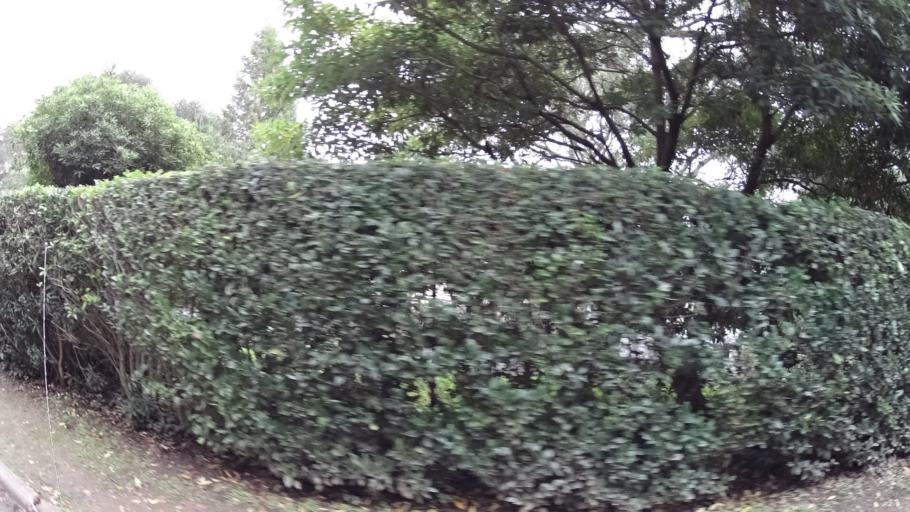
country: US
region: California
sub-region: San Mateo County
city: Hillsborough
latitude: 37.5569
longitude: -122.3612
